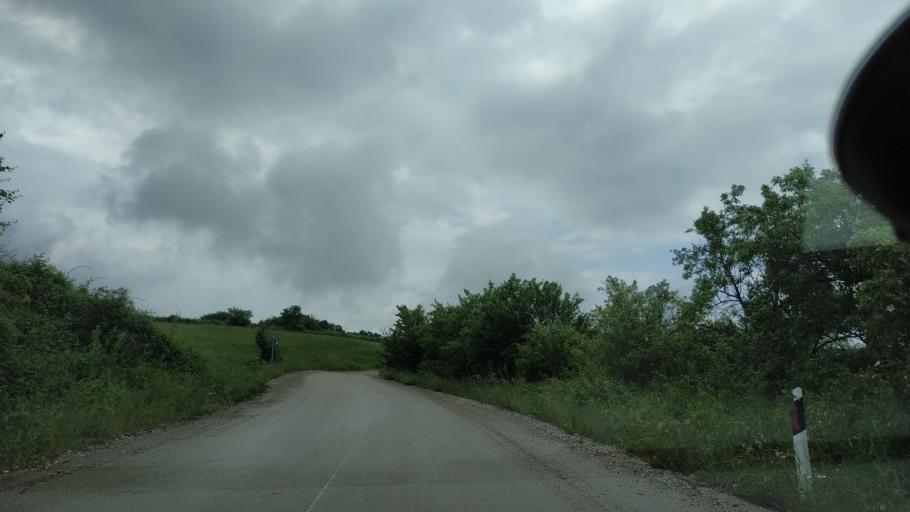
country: RS
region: Central Serbia
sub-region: Toplicki Okrug
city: Prokuplje
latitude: 43.4050
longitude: 21.5598
